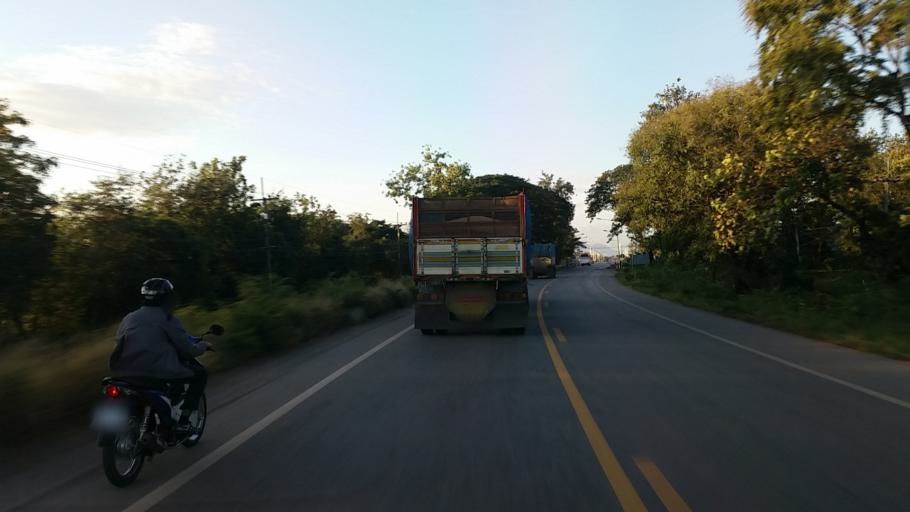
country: TH
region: Lop Buri
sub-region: Amphoe Lam Sonthi
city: Lam Sonthi
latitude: 15.2860
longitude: 101.3500
